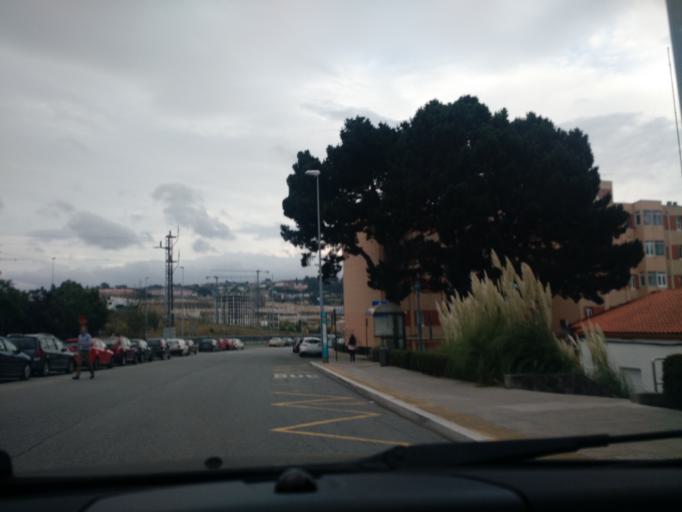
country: ES
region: Galicia
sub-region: Provincia da Coruna
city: A Coruna
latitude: 43.3444
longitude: -8.3993
